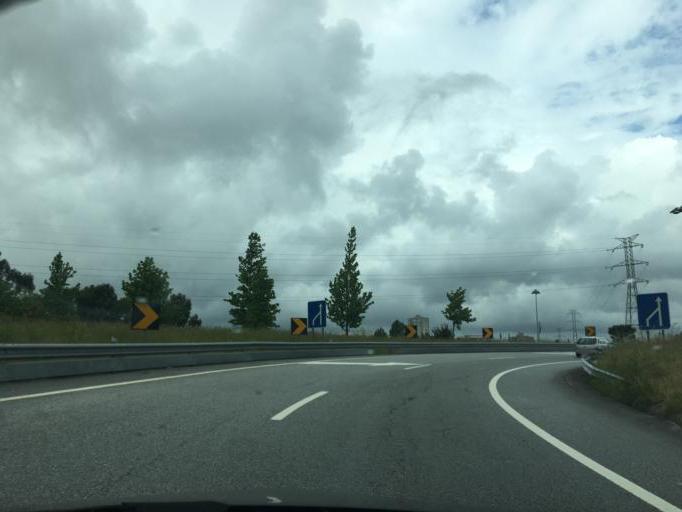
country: PT
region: Porto
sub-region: Porto
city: Porto
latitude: 41.1726
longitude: -8.6236
